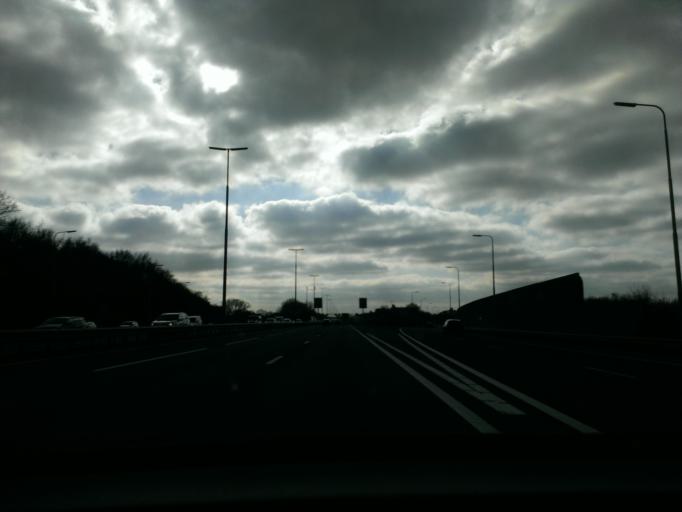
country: NL
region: Overijssel
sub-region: Gemeente Zwolle
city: Zwolle
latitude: 52.5267
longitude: 6.1225
